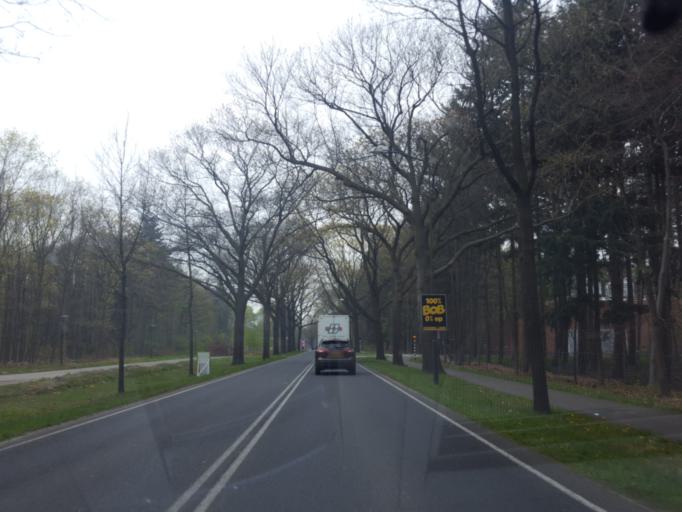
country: NL
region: Gelderland
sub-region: Gemeente Apeldoorn
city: Beekbergen
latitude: 52.1734
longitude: 5.9621
